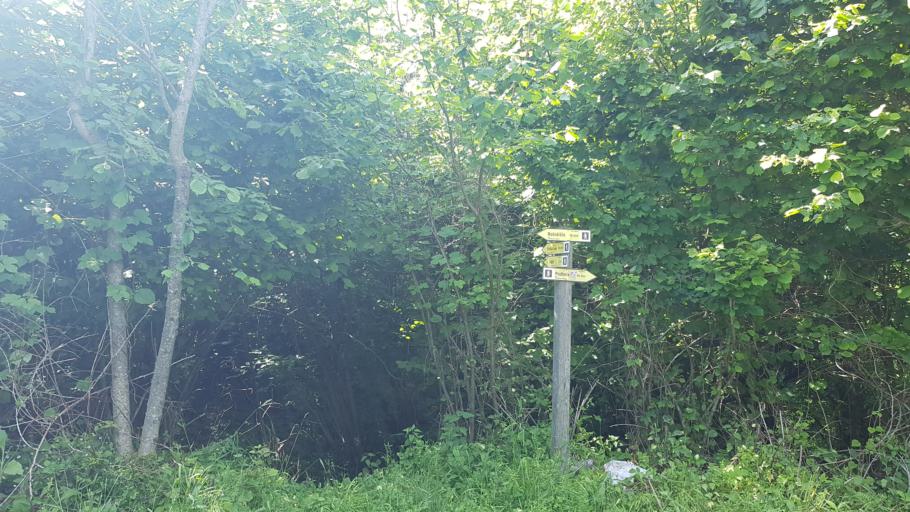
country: IT
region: Friuli Venezia Giulia
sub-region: Provincia di Udine
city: Pulfero
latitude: 46.2195
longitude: 13.4202
